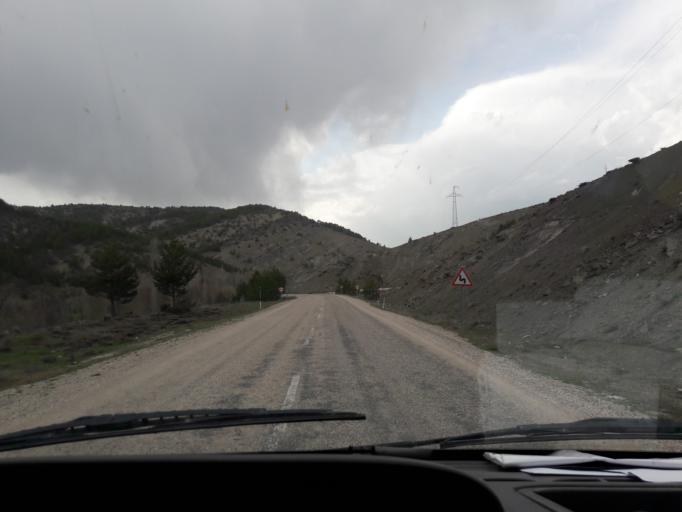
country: TR
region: Giresun
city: Alucra
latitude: 40.2808
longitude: 38.8222
